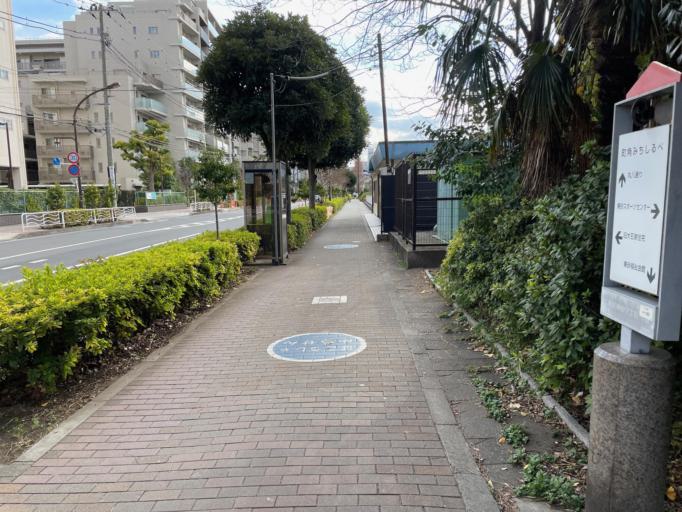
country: JP
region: Tokyo
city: Urayasu
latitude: 35.6757
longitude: 139.8367
